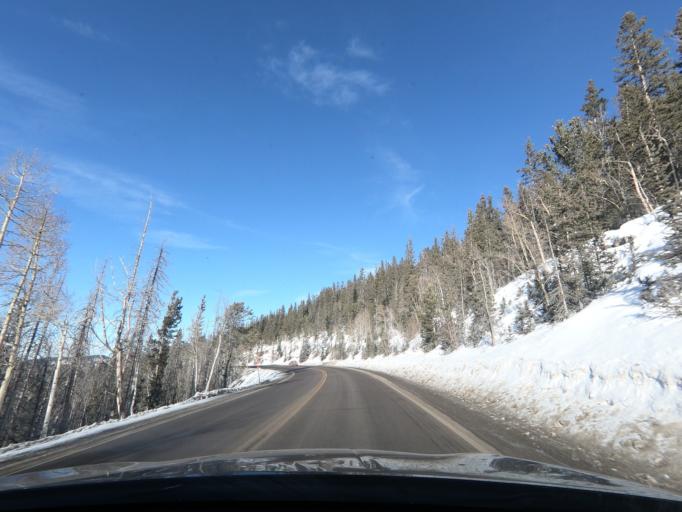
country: US
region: Colorado
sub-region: Teller County
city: Cripple Creek
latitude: 38.7645
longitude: -105.1535
